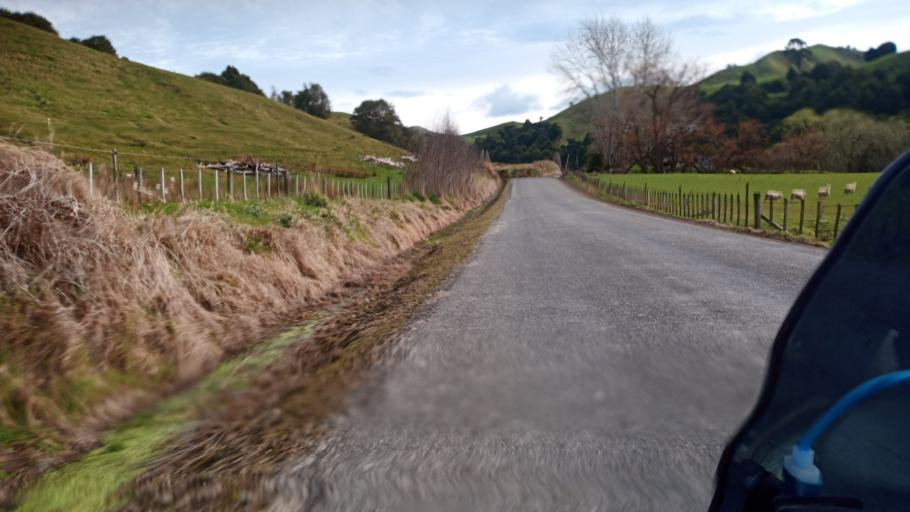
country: NZ
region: Hawke's Bay
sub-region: Wairoa District
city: Wairoa
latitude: -38.7994
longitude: 177.4656
